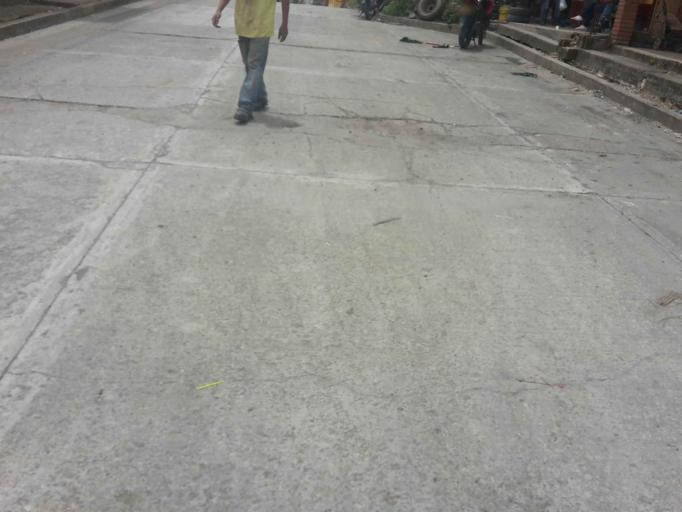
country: CO
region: Cundinamarca
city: Gachala
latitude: 4.6930
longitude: -73.5191
